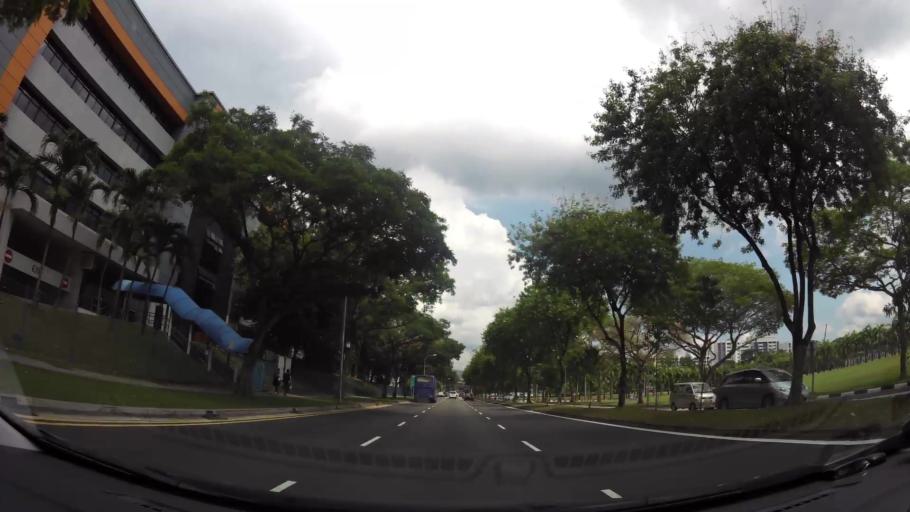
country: MY
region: Johor
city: Johor Bahru
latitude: 1.4395
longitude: 103.7838
